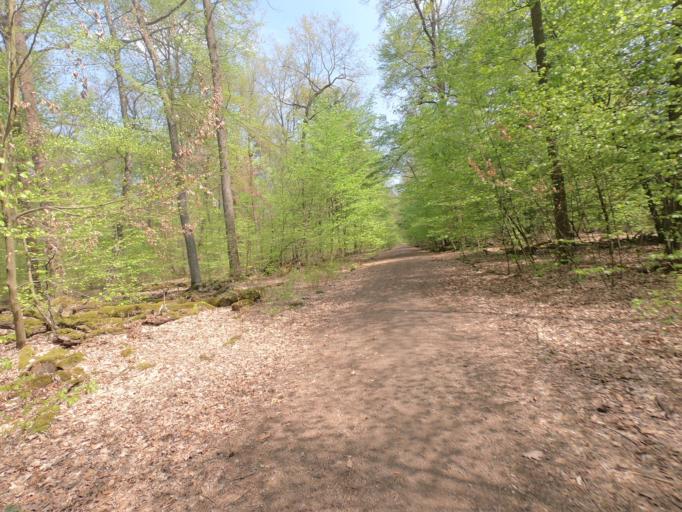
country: DE
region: Hesse
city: Niederrad
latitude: 50.0527
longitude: 8.6399
